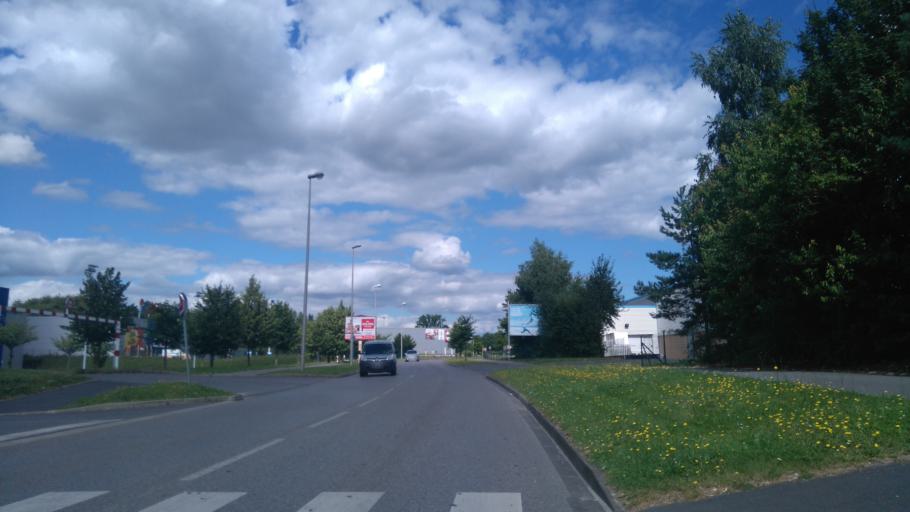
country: FR
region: Picardie
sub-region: Departement de l'Oise
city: Saint-Maximin
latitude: 49.2387
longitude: 2.4669
